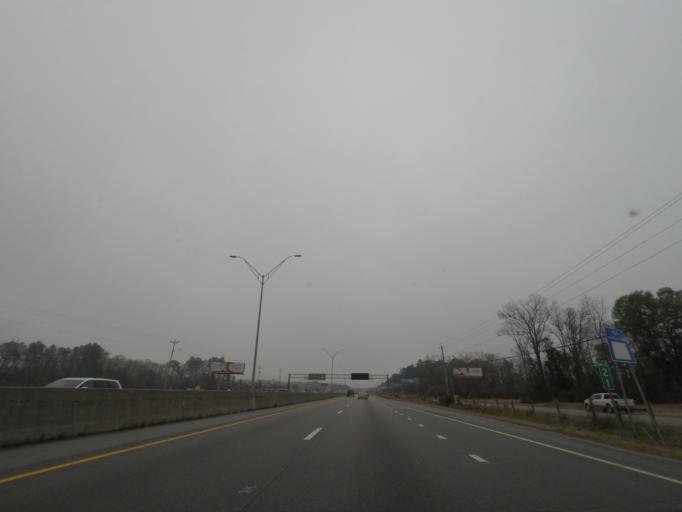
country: US
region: North Carolina
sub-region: Robeson County
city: Lumberton
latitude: 34.6626
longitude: -79.0085
